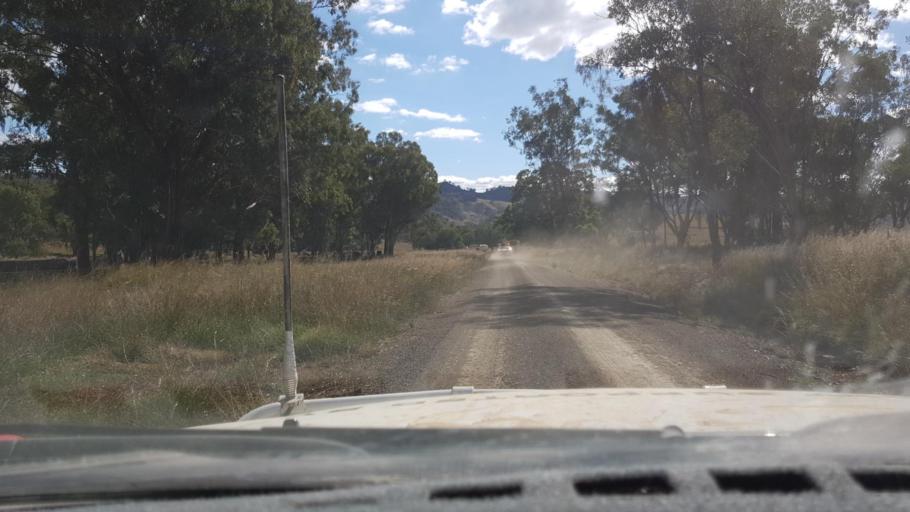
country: AU
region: New South Wales
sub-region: Tamworth Municipality
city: Manilla
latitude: -30.4604
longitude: 150.7803
